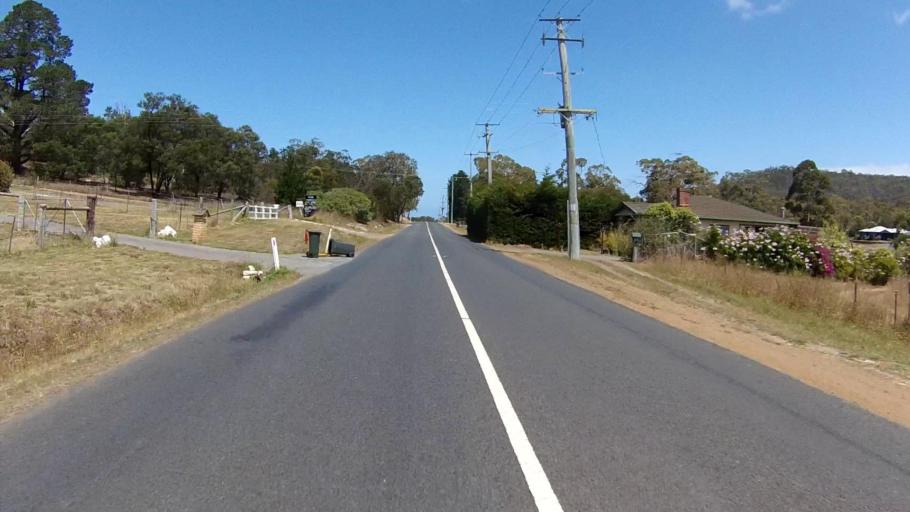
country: AU
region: Tasmania
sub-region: Clarence
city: Sandford
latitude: -42.9598
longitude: 147.4746
